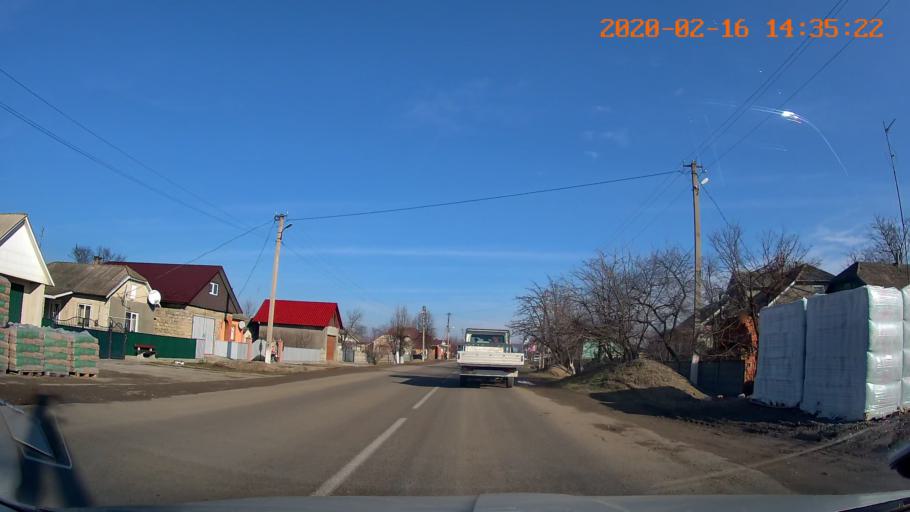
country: RO
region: Botosani
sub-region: Comuna Darabani
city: Bajura
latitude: 48.2230
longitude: 26.4915
